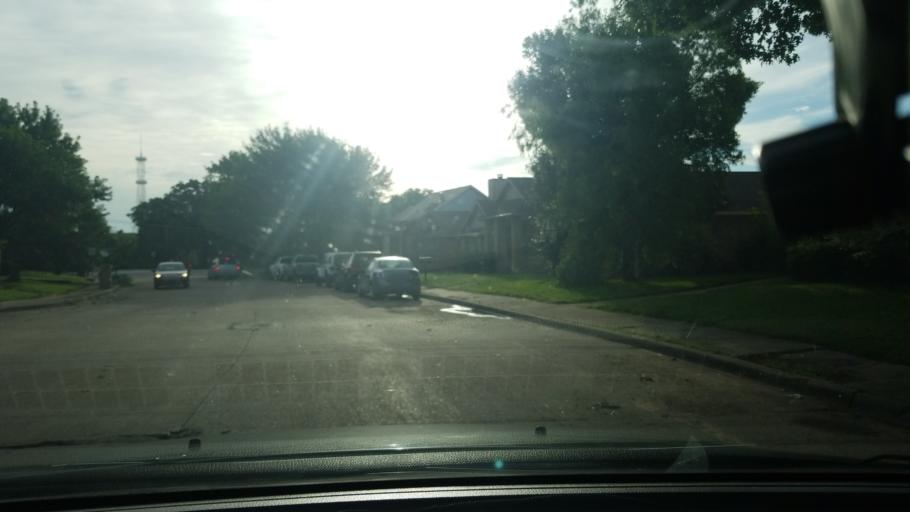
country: US
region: Texas
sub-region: Dallas County
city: Balch Springs
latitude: 32.7576
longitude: -96.6430
